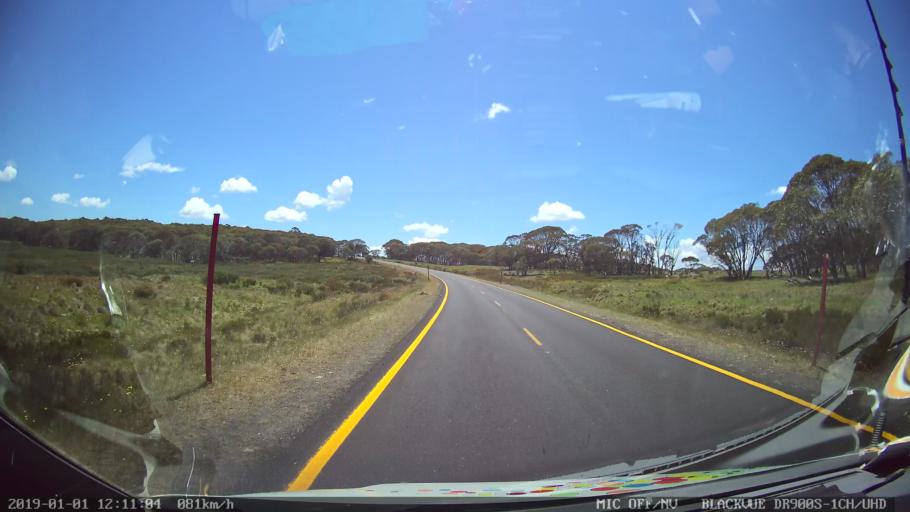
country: AU
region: New South Wales
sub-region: Tumut Shire
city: Tumut
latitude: -35.7879
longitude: 148.5055
